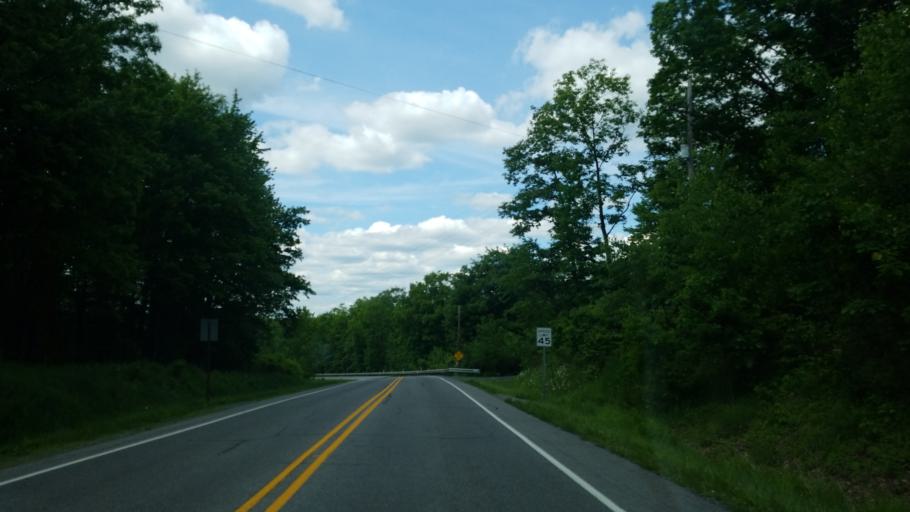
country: US
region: Pennsylvania
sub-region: Clearfield County
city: Clearfield
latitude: 40.9693
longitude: -78.3781
